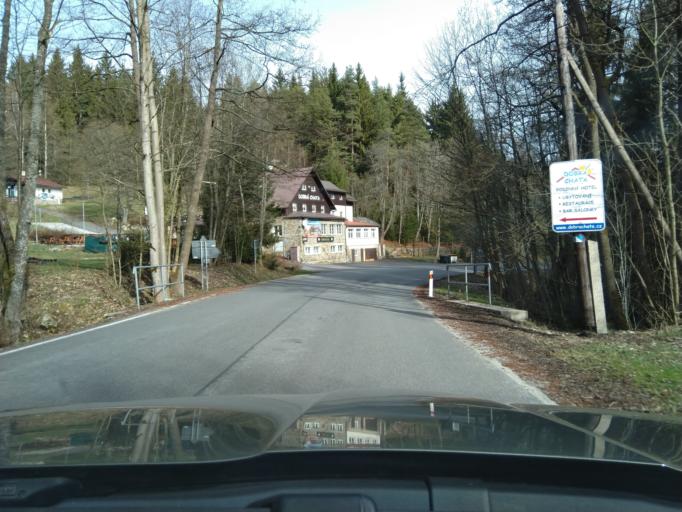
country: CZ
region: Jihocesky
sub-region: Okres Prachatice
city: Stachy
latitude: 49.0727
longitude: 13.6338
